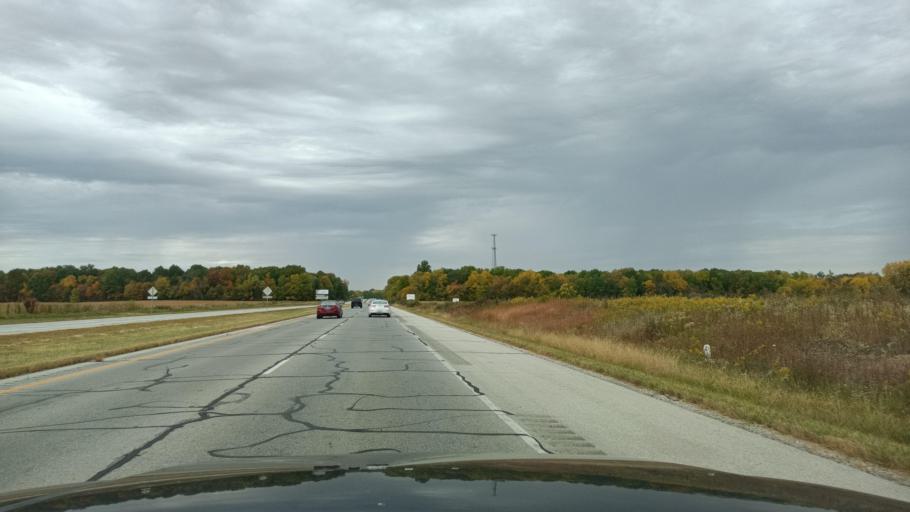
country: US
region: Indiana
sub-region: Delaware County
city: Yorktown
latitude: 40.2193
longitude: -85.5029
